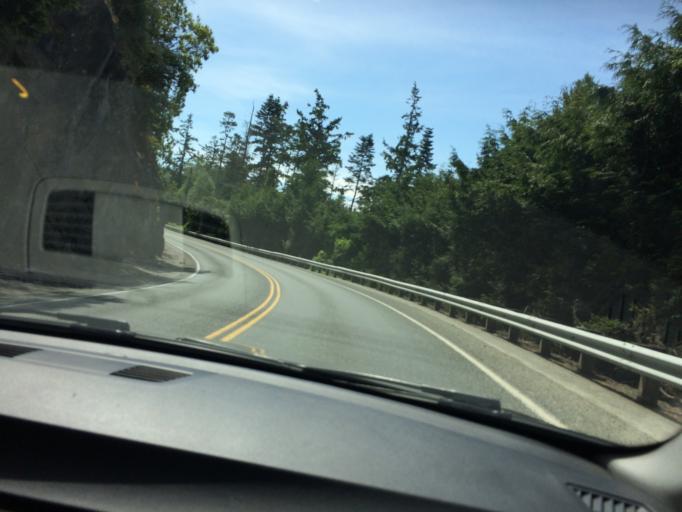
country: US
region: Washington
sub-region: Skagit County
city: Anacortes
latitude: 48.4615
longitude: -122.6549
